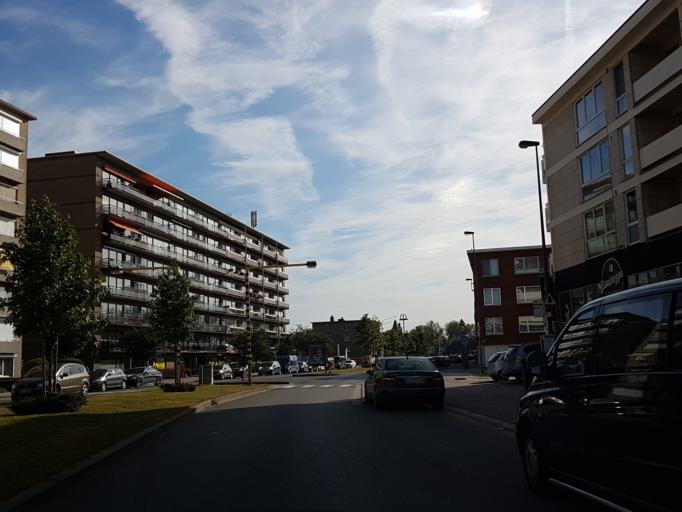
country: BE
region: Flanders
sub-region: Provincie Antwerpen
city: Antwerpen
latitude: 51.2470
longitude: 4.4314
